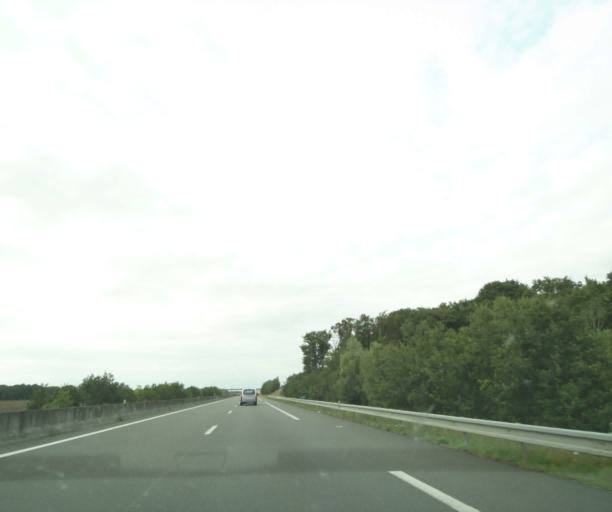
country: FR
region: Centre
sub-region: Departement d'Indre-et-Loire
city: Saint-Antoine-du-Rocher
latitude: 47.5076
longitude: 0.6373
